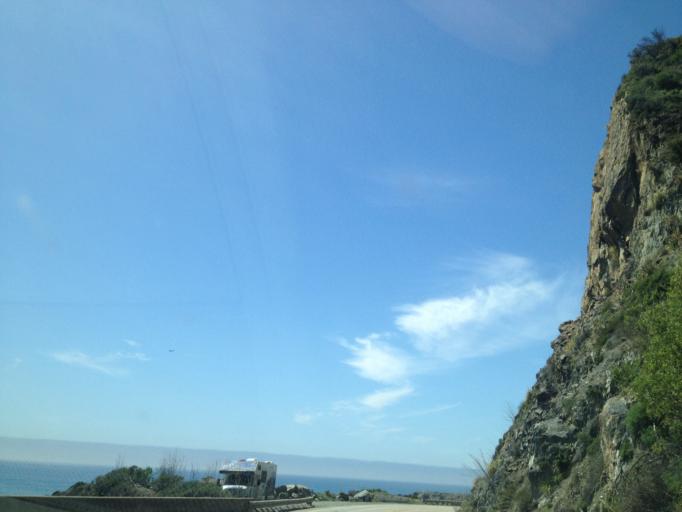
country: US
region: California
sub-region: Monterey County
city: Greenfield
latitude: 36.0080
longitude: -121.5142
